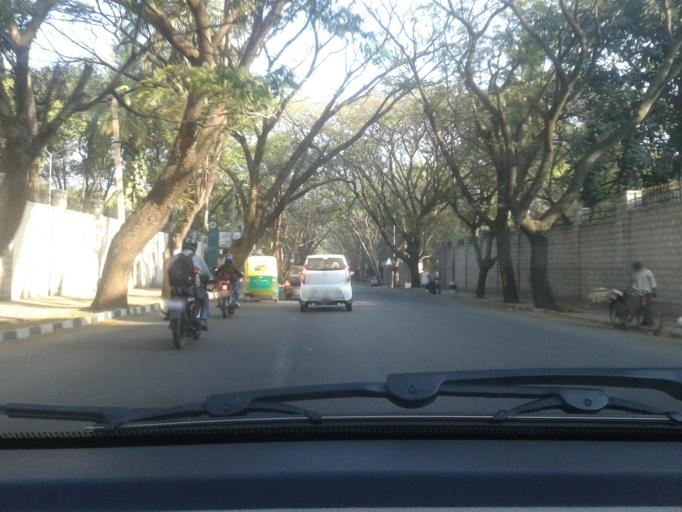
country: IN
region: Karnataka
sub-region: Bangalore Urban
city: Bangalore
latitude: 13.0215
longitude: 77.5723
